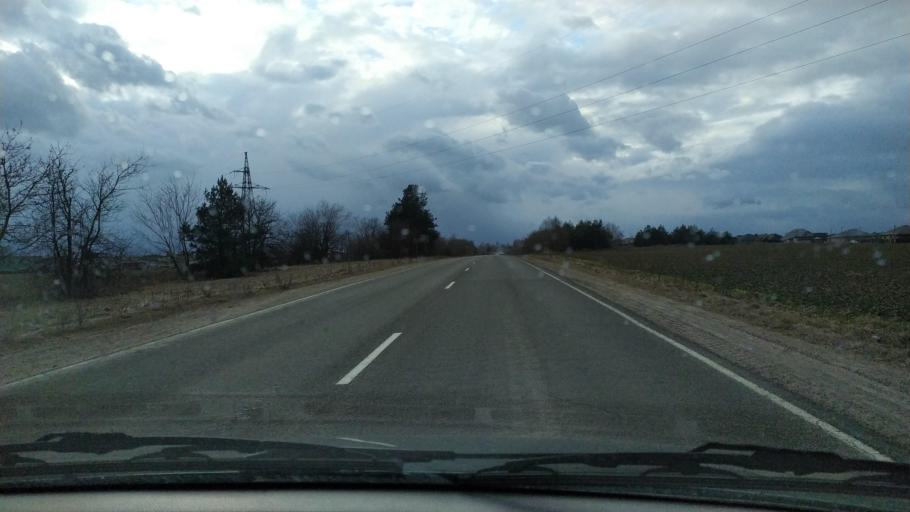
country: BY
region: Brest
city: Kamyanyets
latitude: 52.4020
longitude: 23.8532
